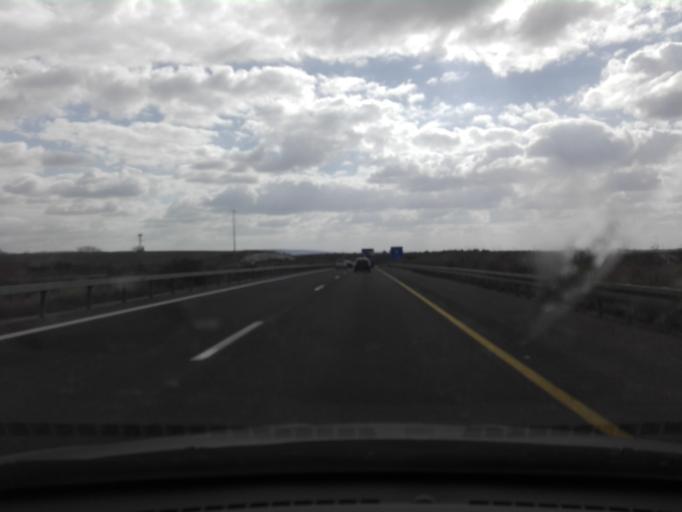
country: IL
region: Haifa
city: El Fureidis
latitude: 32.5938
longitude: 35.0457
